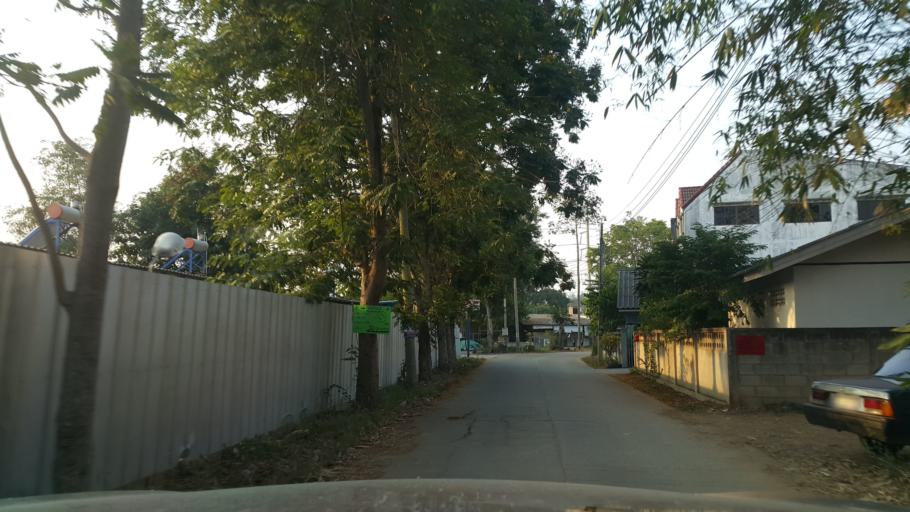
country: TH
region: Chiang Mai
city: Saraphi
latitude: 18.7252
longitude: 99.0174
